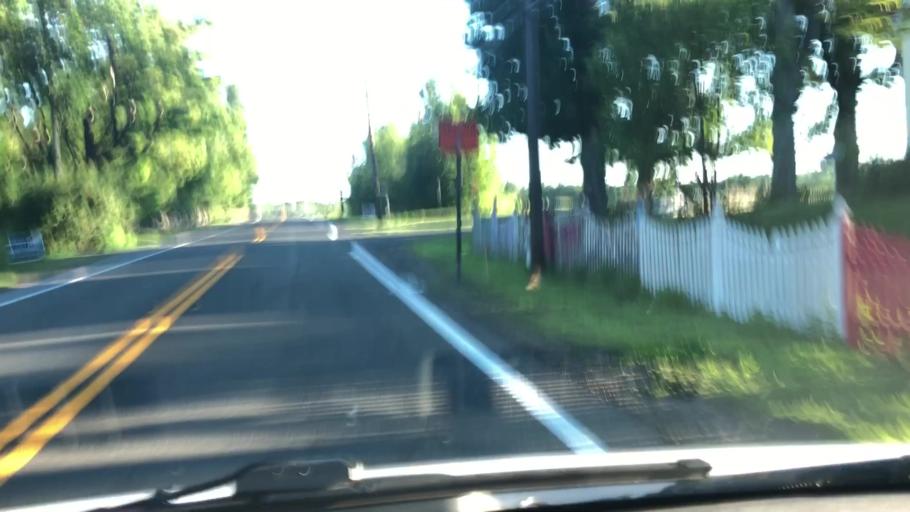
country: US
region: Massachusetts
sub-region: Hampshire County
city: Chesterfield
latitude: 42.3862
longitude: -72.9300
